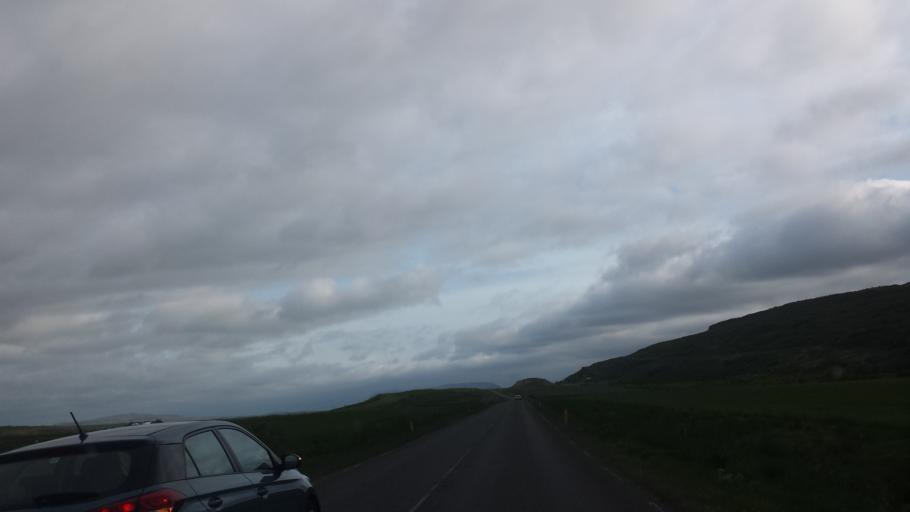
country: IS
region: South
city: Selfoss
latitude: 64.2113
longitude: -20.3793
